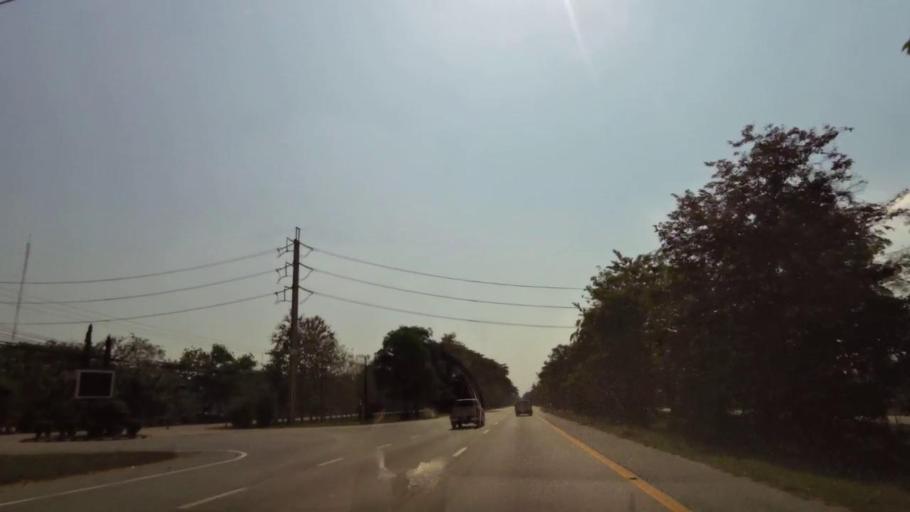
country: TH
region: Phichit
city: Wachira Barami
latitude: 16.5753
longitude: 100.1482
